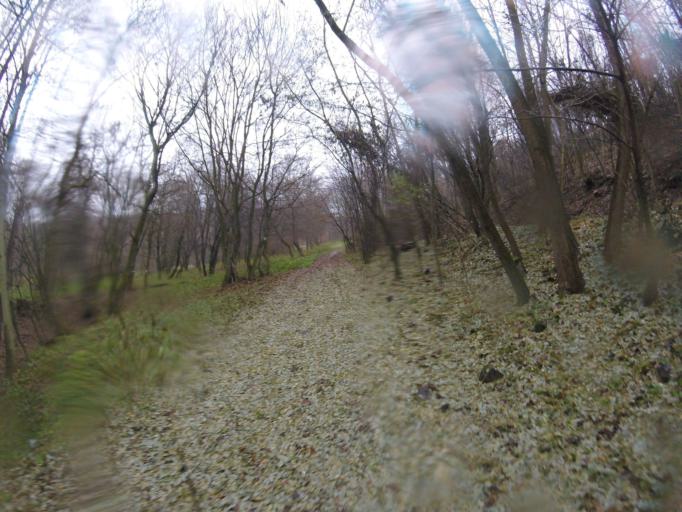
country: HU
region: Pest
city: Szob
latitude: 47.8523
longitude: 18.8474
